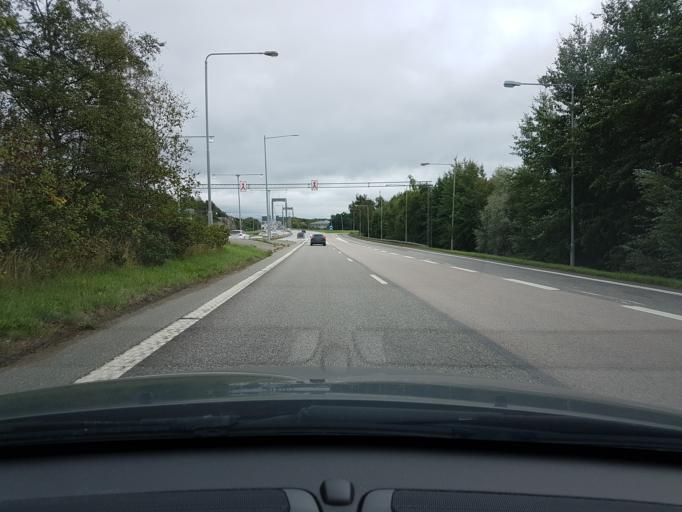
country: SE
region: Vaestra Goetaland
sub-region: Goteborg
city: Majorna
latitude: 57.7026
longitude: 11.8931
